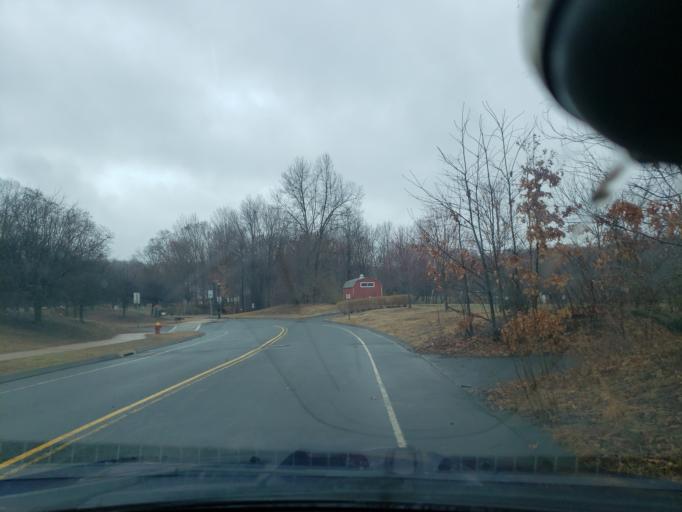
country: US
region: Connecticut
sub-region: Hartford County
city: Tariffville
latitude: 41.8979
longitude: -72.7013
